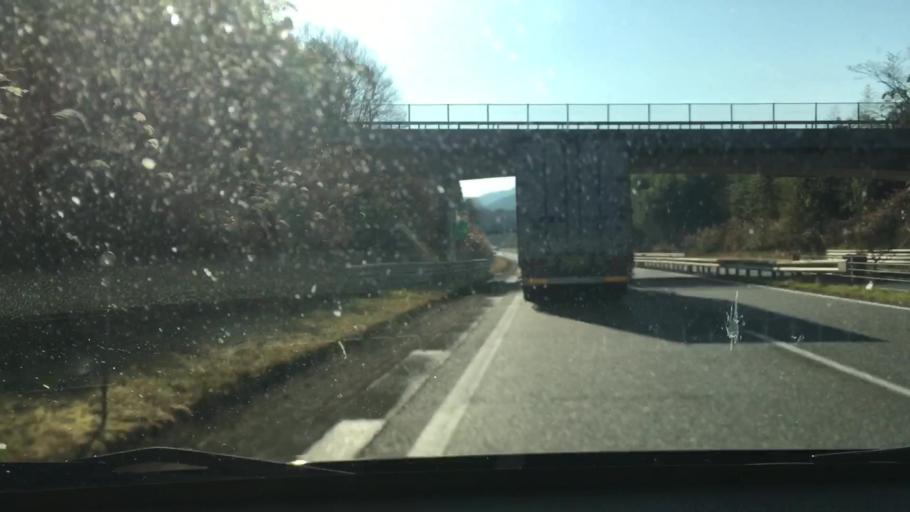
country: JP
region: Kagoshima
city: Okuchi-shinohara
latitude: 31.9425
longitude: 130.7163
